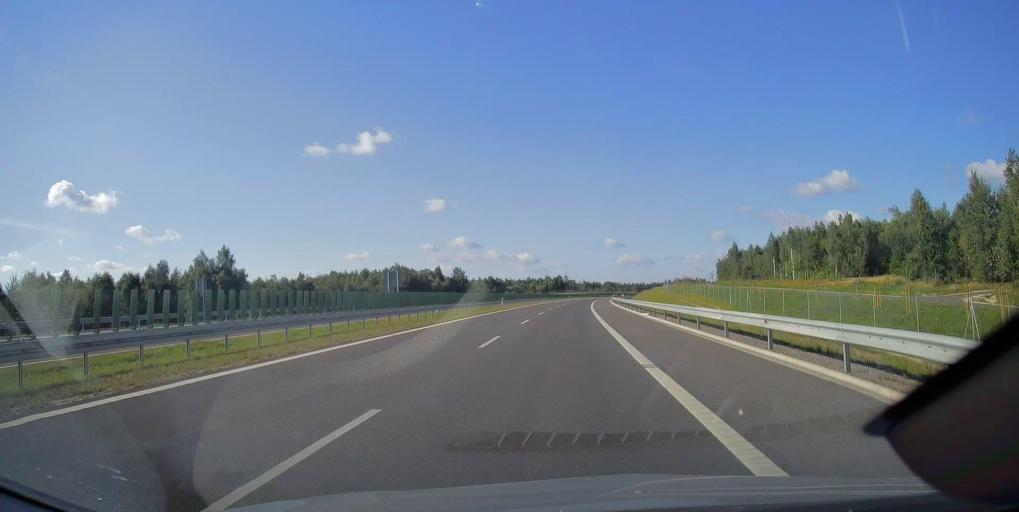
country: PL
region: Swietokrzyskie
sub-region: Powiat skarzyski
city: Skarzysko-Kamienna
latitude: 51.1369
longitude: 20.8327
